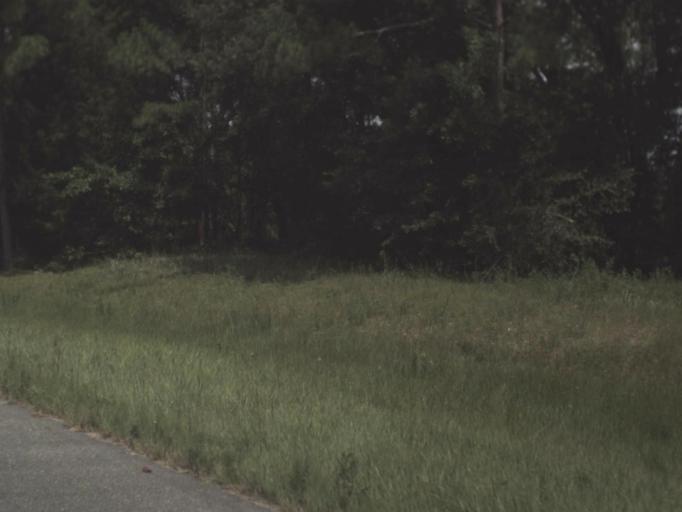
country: US
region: Florida
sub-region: Madison County
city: Madison
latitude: 30.4882
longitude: -83.4909
